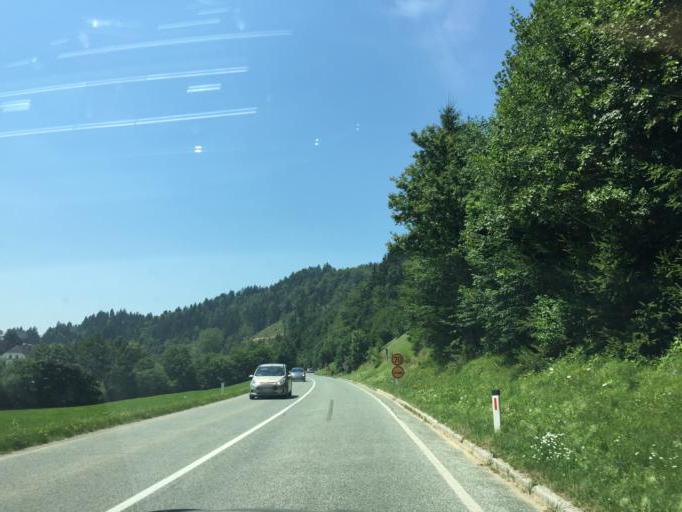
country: SI
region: Gorenja Vas-Poljane
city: Gorenja Vas
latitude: 46.1284
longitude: 14.2123
